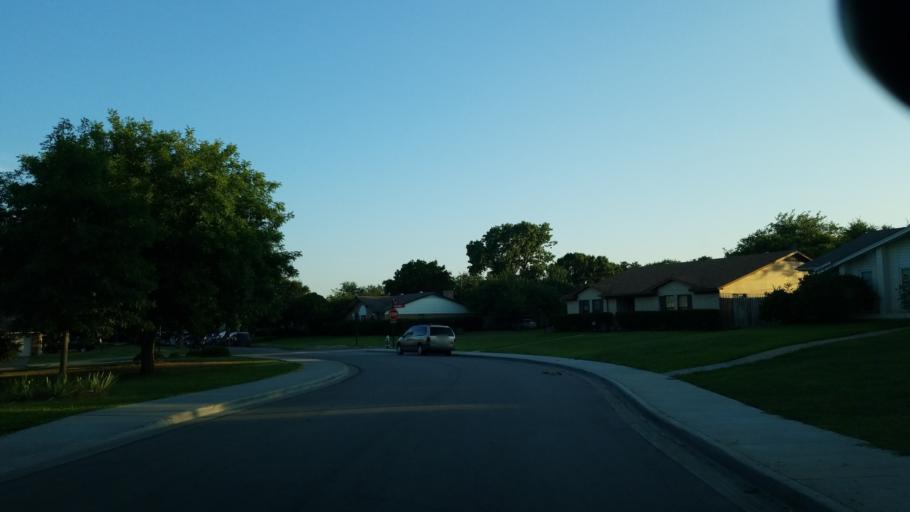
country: US
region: Texas
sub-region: Dallas County
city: Carrollton
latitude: 32.9437
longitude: -96.8854
